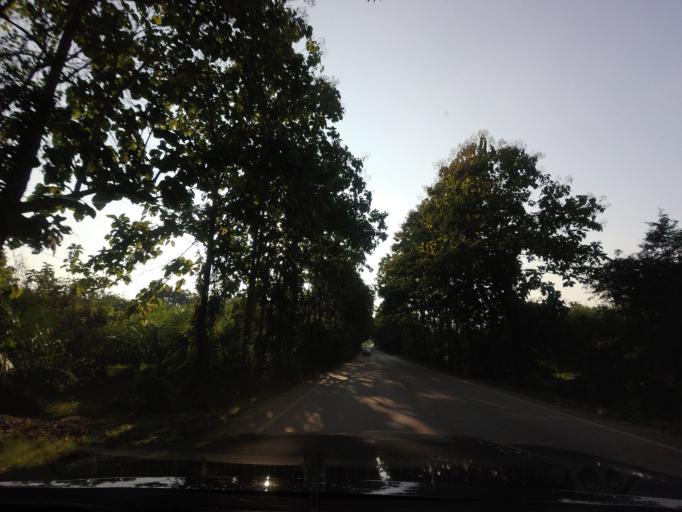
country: TH
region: Nan
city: Na Noi
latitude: 18.3347
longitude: 100.7577
